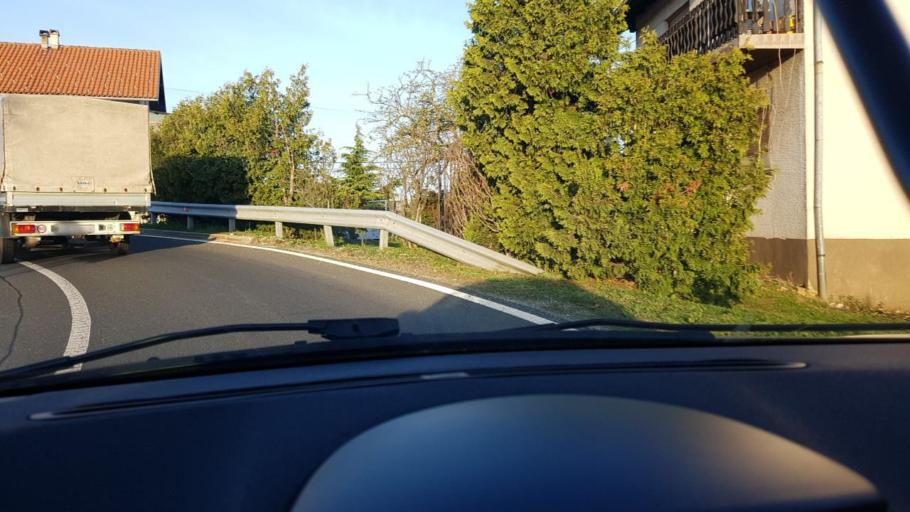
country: HR
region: Krapinsko-Zagorska
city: Marija Bistrica
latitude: 45.9726
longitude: 16.0983
